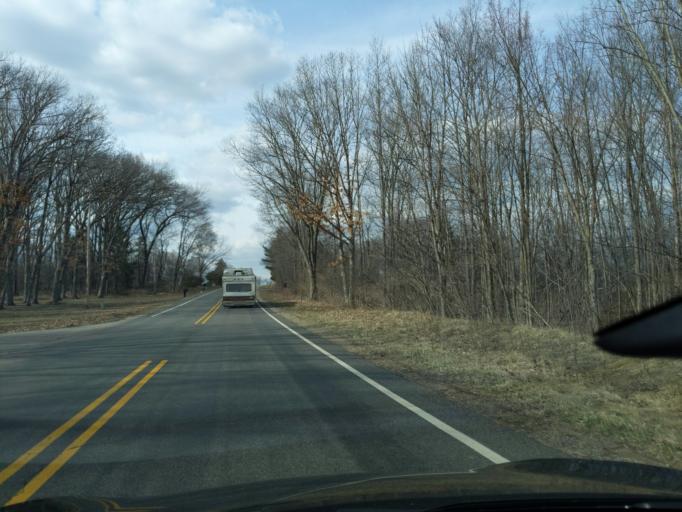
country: US
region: Michigan
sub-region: Ingham County
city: Leslie
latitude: 42.3549
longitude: -84.4177
